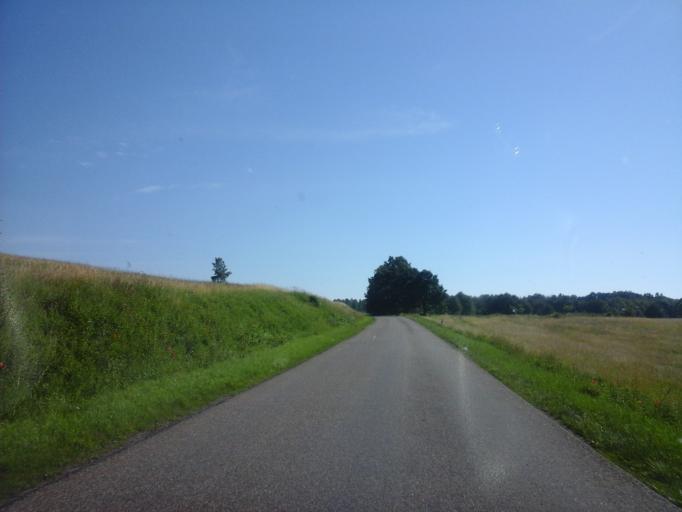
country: PL
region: West Pomeranian Voivodeship
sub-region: Powiat drawski
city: Zlocieniec
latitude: 53.6419
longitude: 16.0078
